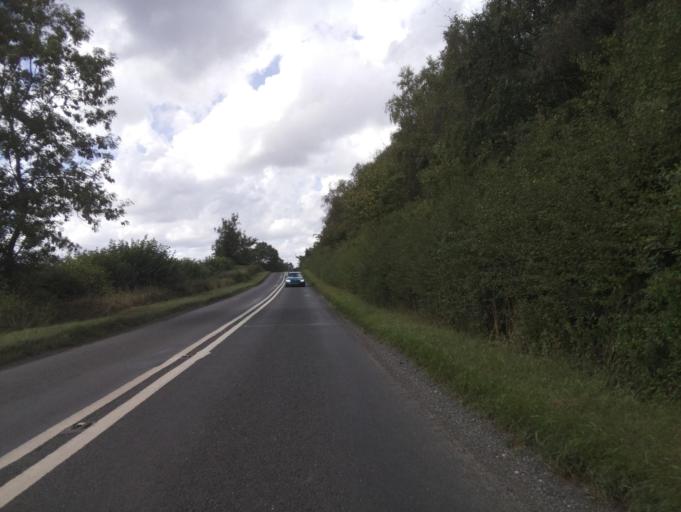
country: GB
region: England
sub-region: North Yorkshire
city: Bedale
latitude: 54.2375
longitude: -1.6775
